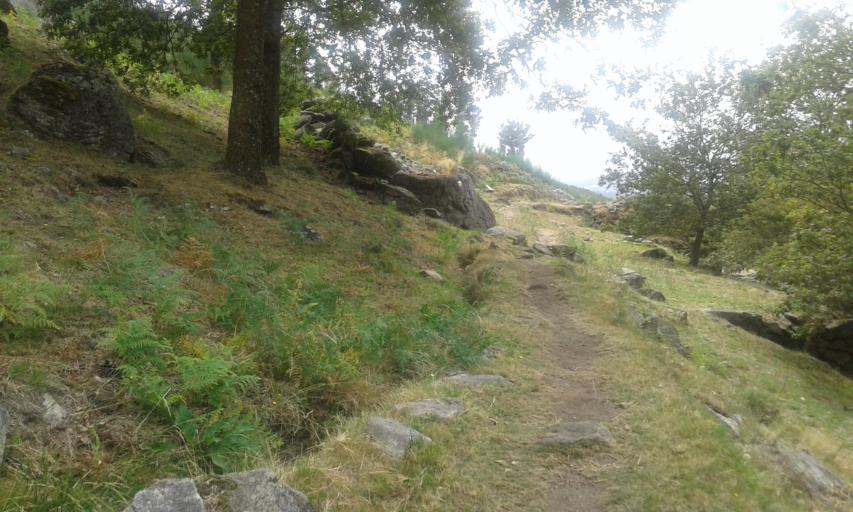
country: ES
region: Galicia
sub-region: Provincia de Pontevedra
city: O Rosal
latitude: 41.9613
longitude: -8.8403
